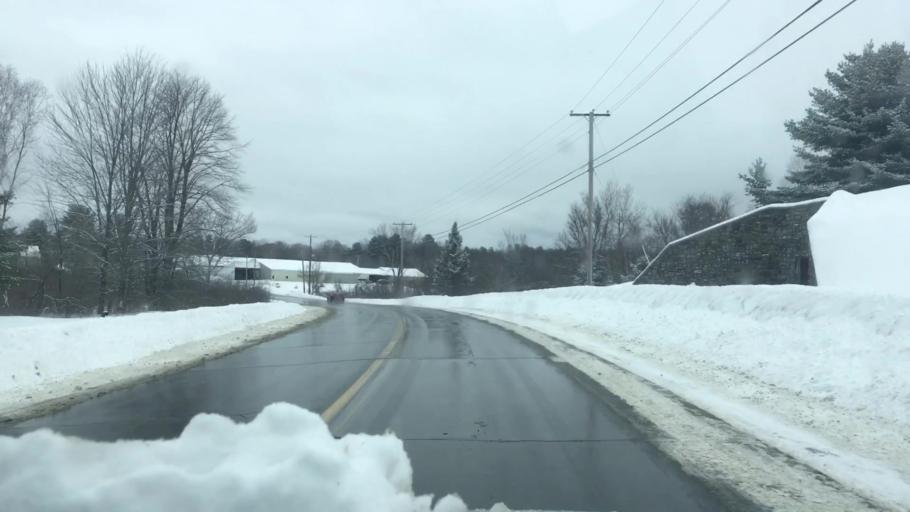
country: US
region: Maine
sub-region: Penobscot County
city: Charleston
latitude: 44.9964
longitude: -69.0387
